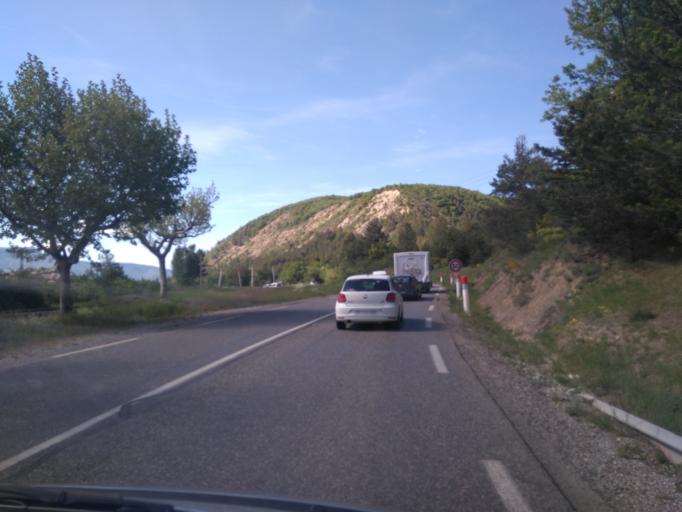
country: FR
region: Provence-Alpes-Cote d'Azur
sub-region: Departement des Hautes-Alpes
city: Laragne-Monteglin
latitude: 44.3317
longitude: 5.7888
